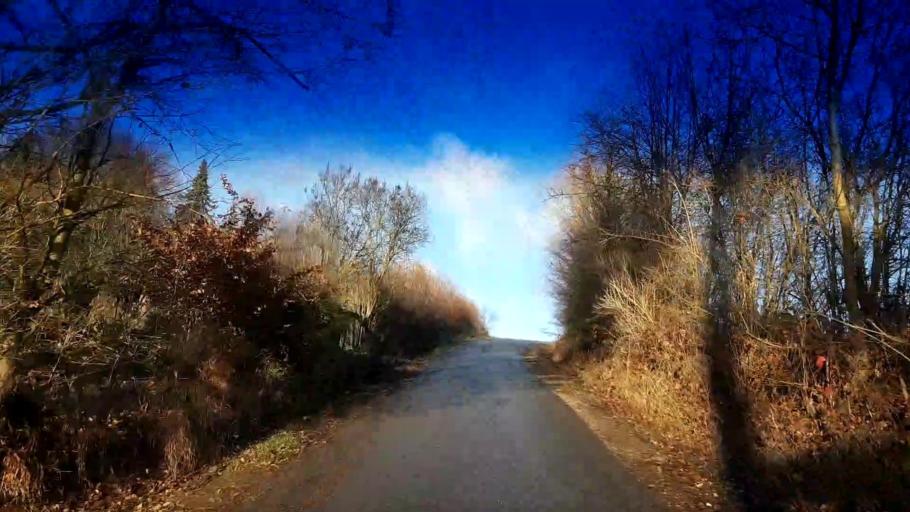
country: DE
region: Bavaria
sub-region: Upper Franconia
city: Pettstadt
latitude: 49.8371
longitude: 10.9206
